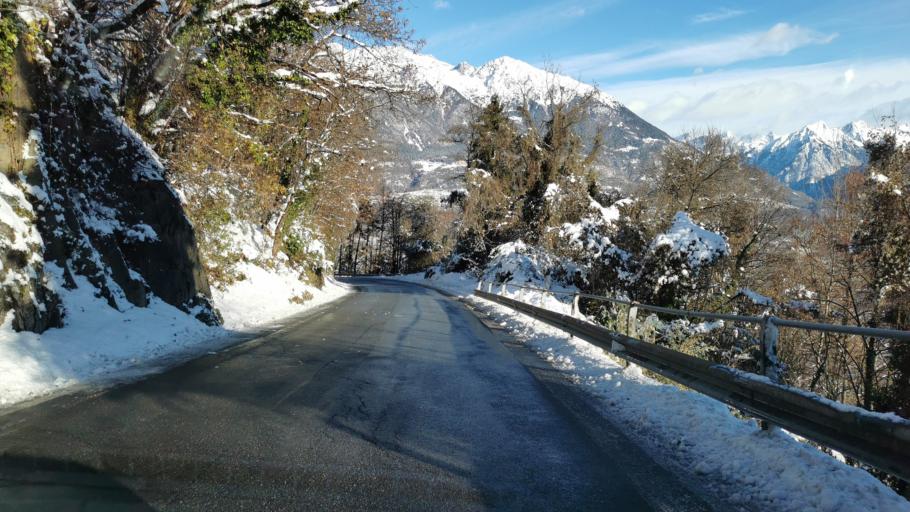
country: IT
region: Lombardy
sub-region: Provincia di Sondrio
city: Bema
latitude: 46.1192
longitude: 9.5609
